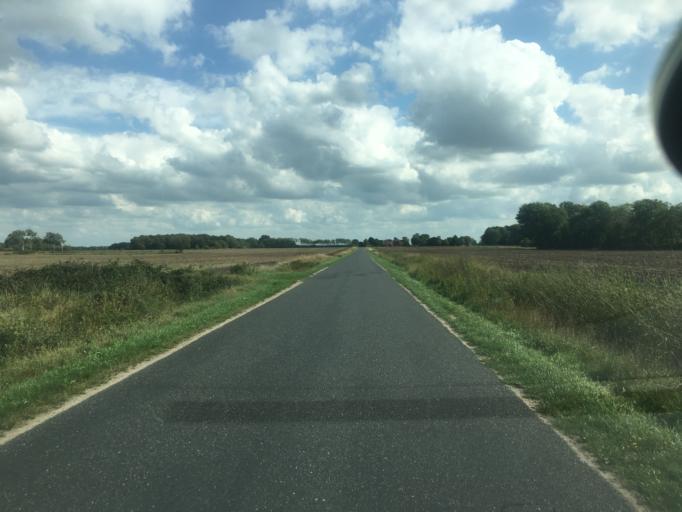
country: DK
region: South Denmark
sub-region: Tonder Kommune
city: Logumkloster
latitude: 55.0193
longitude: 8.9914
